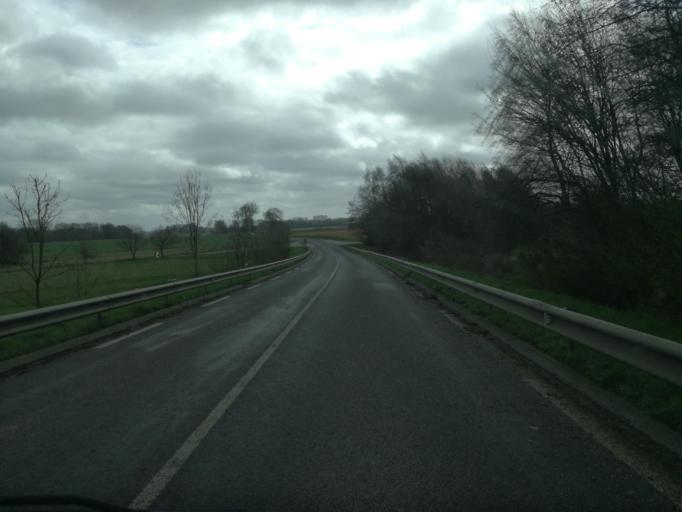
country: FR
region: Haute-Normandie
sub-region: Departement de la Seine-Maritime
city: Valliquerville
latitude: 49.6283
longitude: 0.6420
